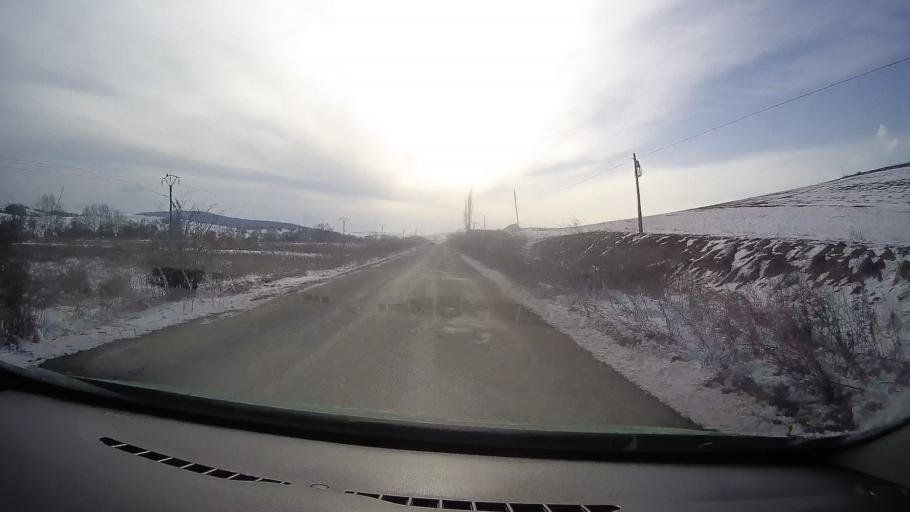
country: RO
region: Sibiu
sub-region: Oras Agnita
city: Ruja
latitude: 46.0133
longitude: 24.6882
